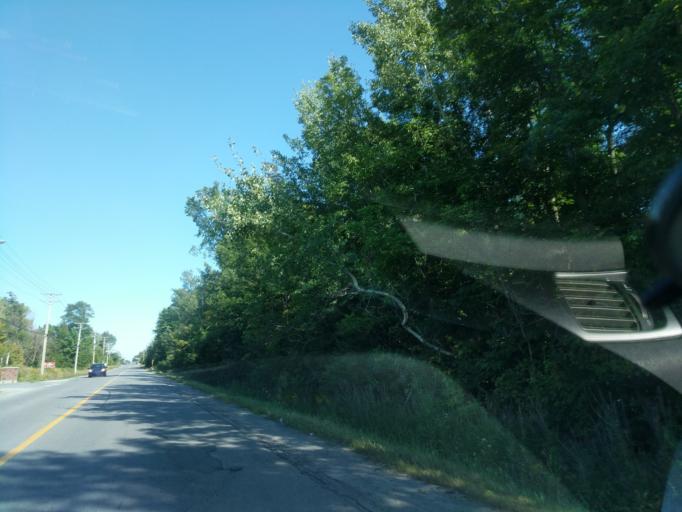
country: CA
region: Ontario
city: Bells Corners
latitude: 45.4119
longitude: -75.8150
